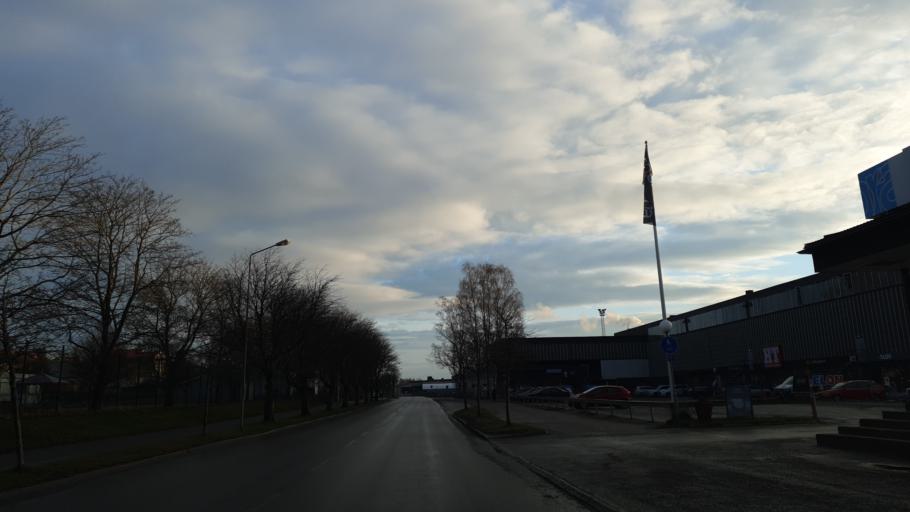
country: SE
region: Gaevleborg
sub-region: Hudiksvalls Kommun
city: Hudiksvall
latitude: 61.7255
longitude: 17.1274
